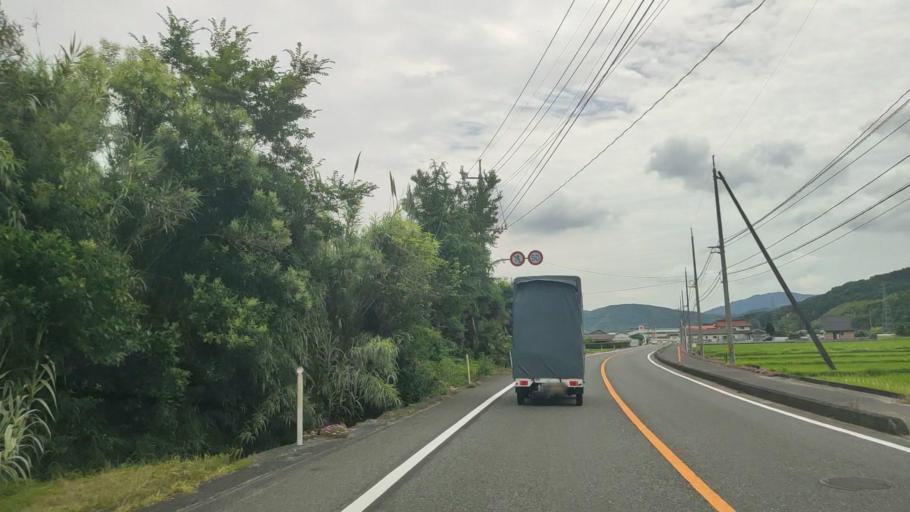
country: JP
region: Okayama
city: Tsuyama
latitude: 35.0552
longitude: 133.9132
